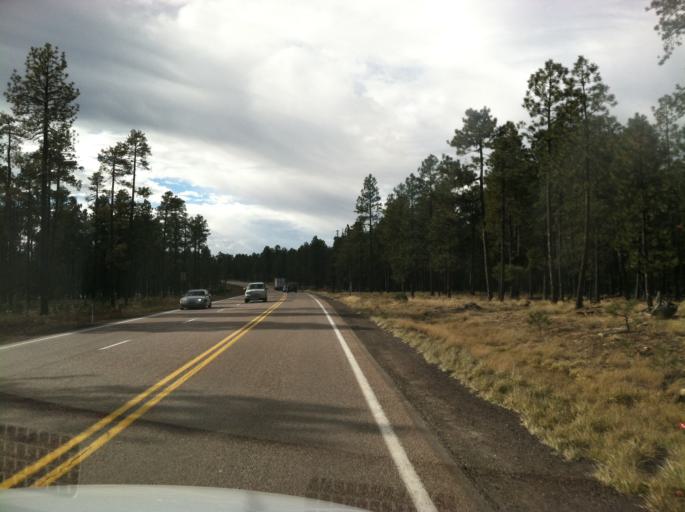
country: US
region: Arizona
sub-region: Navajo County
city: Heber-Overgaard
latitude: 34.3111
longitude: -110.8532
